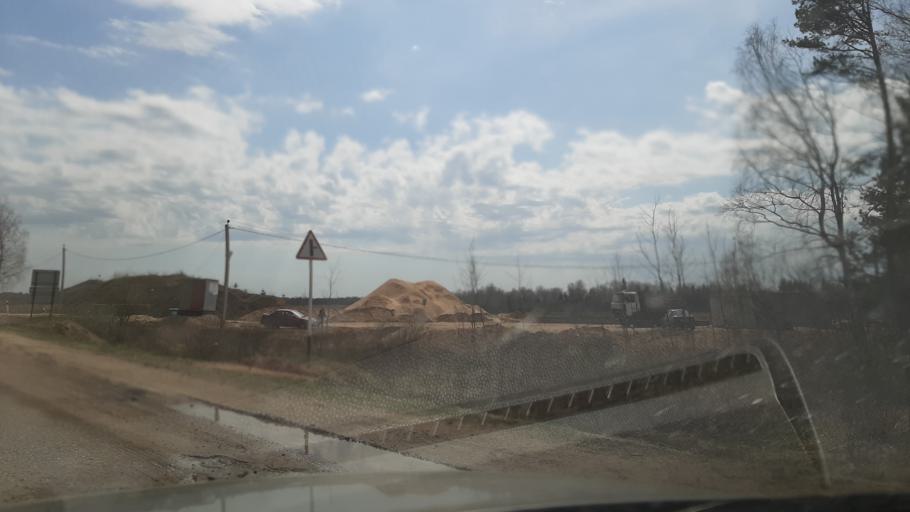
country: RU
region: Ivanovo
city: Furmanov
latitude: 57.1716
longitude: 41.0628
